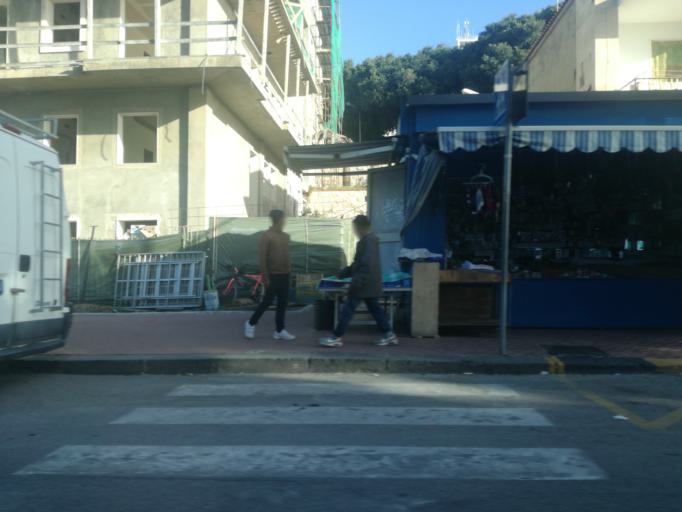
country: IT
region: Sicily
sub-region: Provincia di Caltanissetta
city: Gela
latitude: 37.0639
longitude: 14.2491
